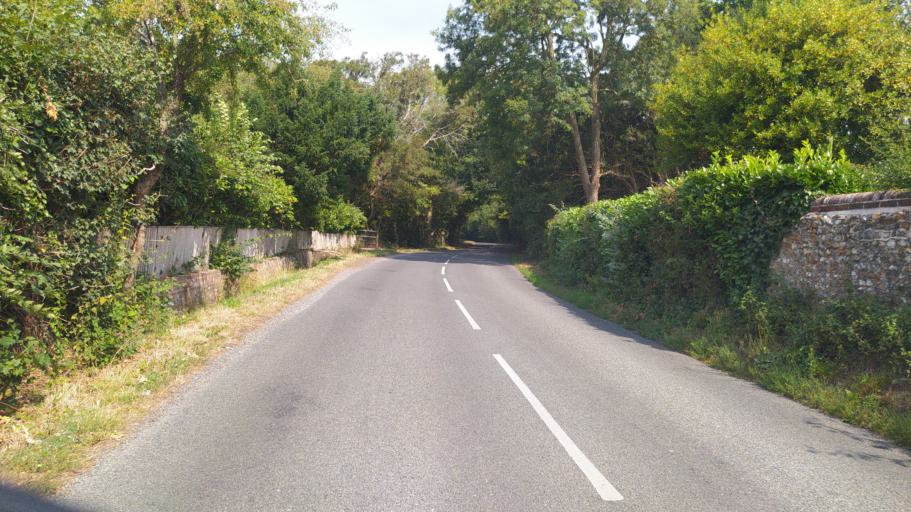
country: GB
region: England
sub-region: Hampshire
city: Emsworth
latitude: 50.8638
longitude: -0.9551
